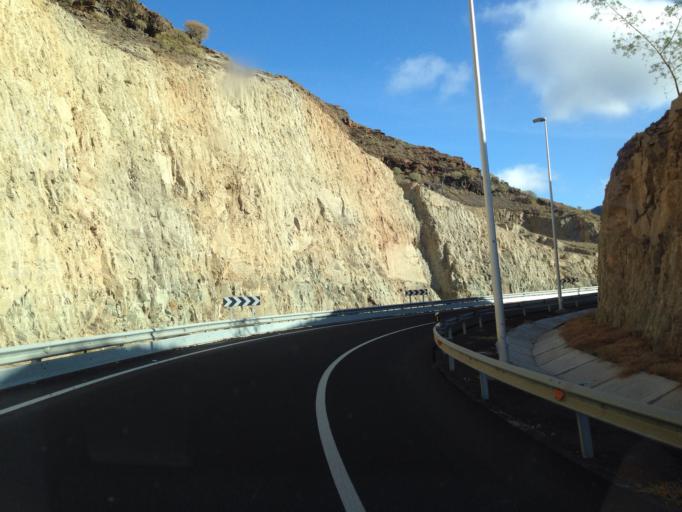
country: ES
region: Canary Islands
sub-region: Provincia de Las Palmas
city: Puerto Rico
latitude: 27.8259
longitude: -15.7478
